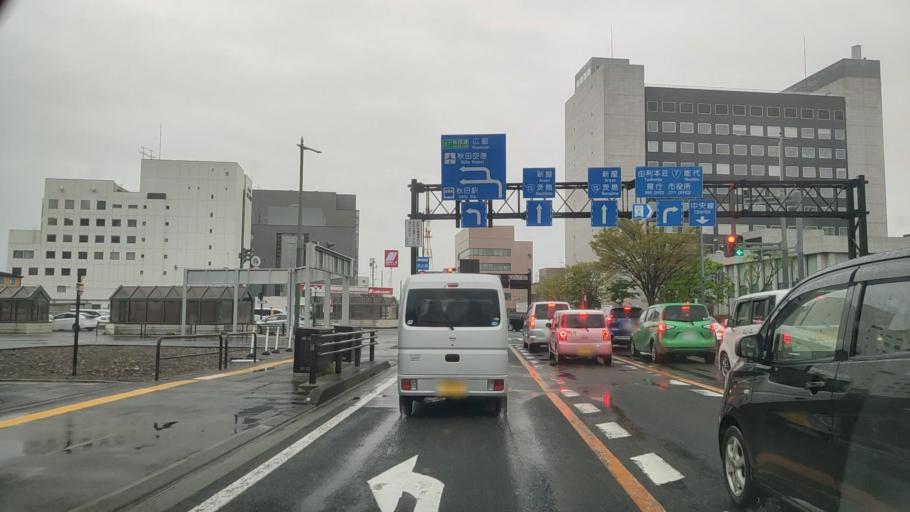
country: JP
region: Akita
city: Akita Shi
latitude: 39.7199
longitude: 140.1084
